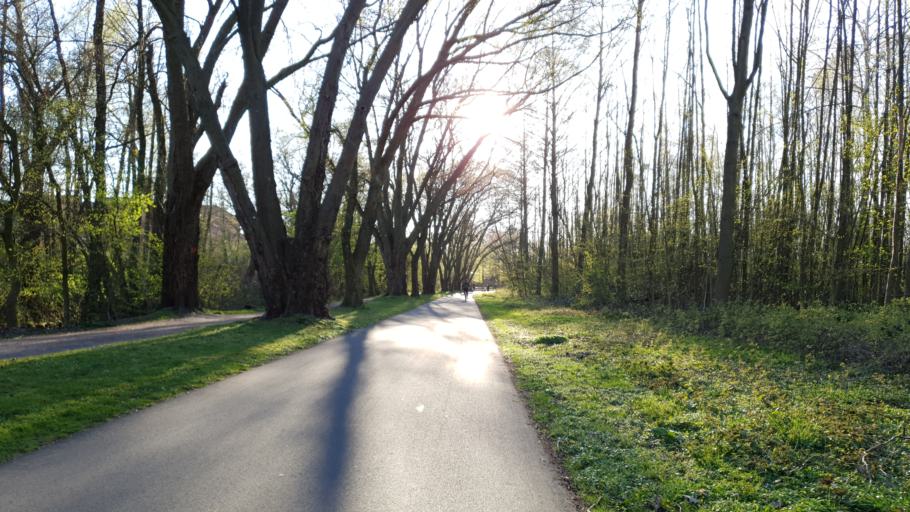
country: DE
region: North Rhine-Westphalia
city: Opladen
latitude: 51.0414
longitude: 7.0165
